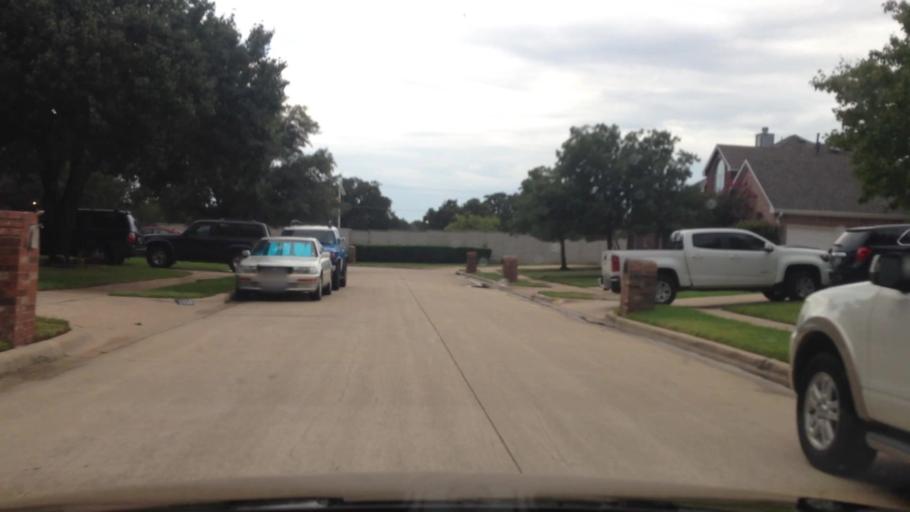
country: US
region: Texas
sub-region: Denton County
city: Flower Mound
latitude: 33.0148
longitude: -97.0525
